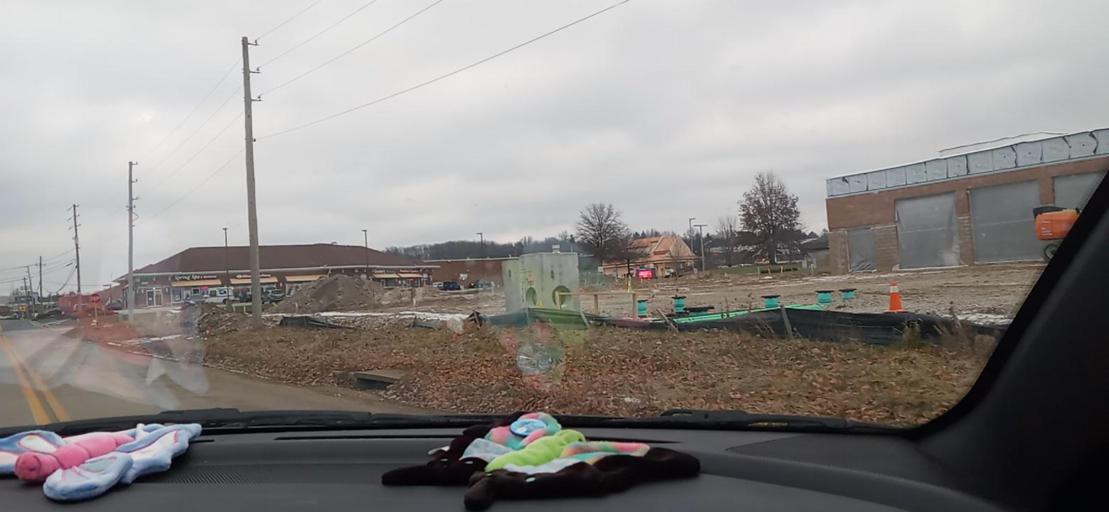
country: US
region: Ohio
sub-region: Summit County
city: Montrose-Ghent
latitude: 41.1326
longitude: -81.6394
